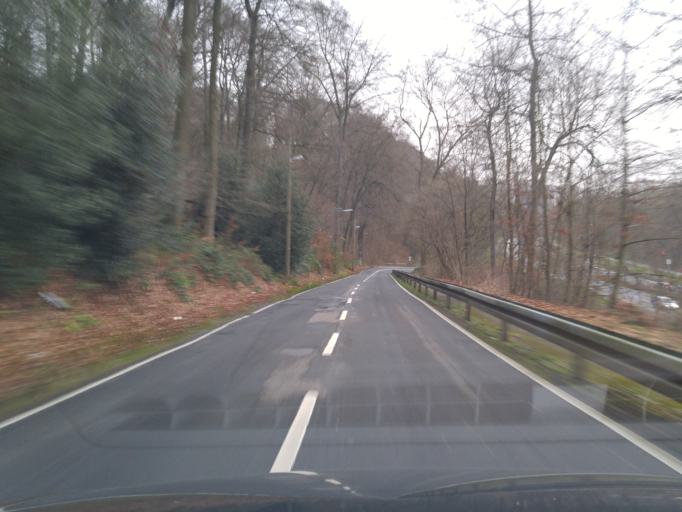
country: DE
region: North Rhine-Westphalia
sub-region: Regierungsbezirk Dusseldorf
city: Essen
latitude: 51.4180
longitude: 7.0633
